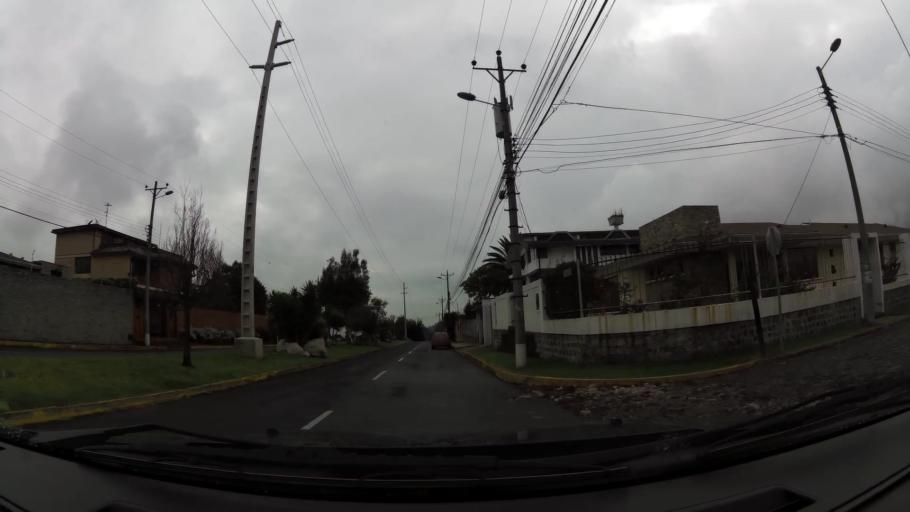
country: EC
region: Pichincha
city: Sangolqui
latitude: -0.2661
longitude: -78.4597
